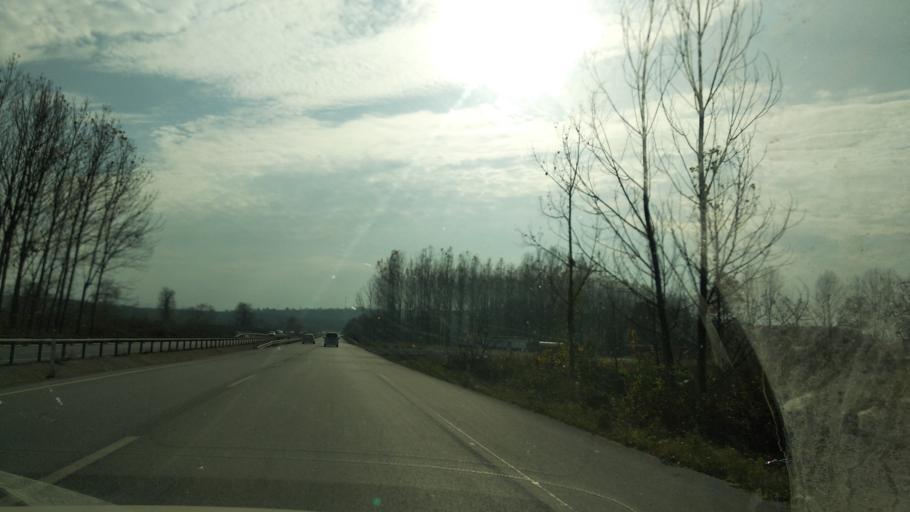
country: TR
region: Sakarya
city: Karasu
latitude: 41.0598
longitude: 30.6369
